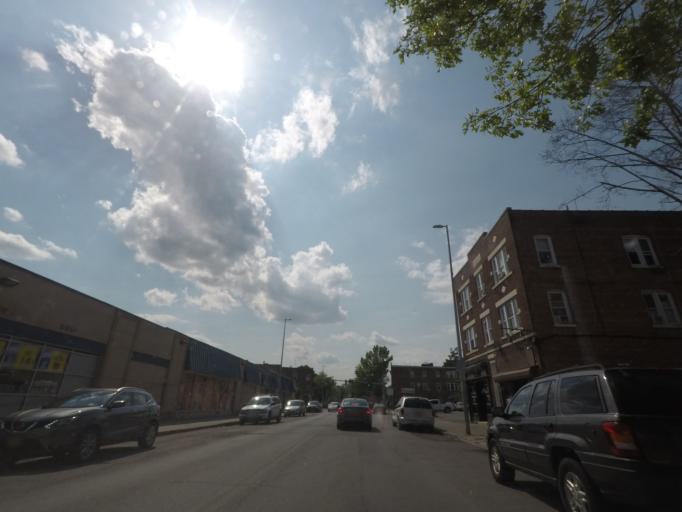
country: US
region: New York
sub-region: Dutchess County
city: Poughkeepsie
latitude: 41.6978
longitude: -73.9101
